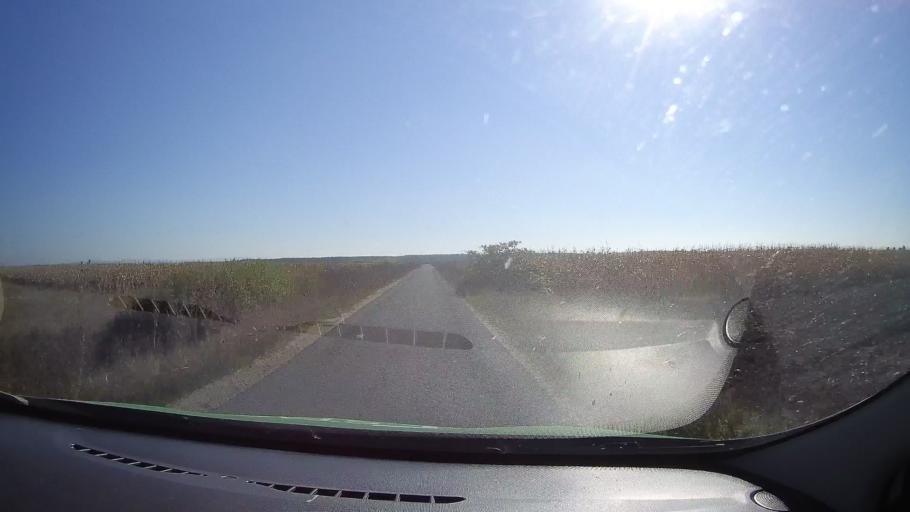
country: RO
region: Satu Mare
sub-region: Comuna Doba
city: Doba
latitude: 47.7342
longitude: 22.7221
